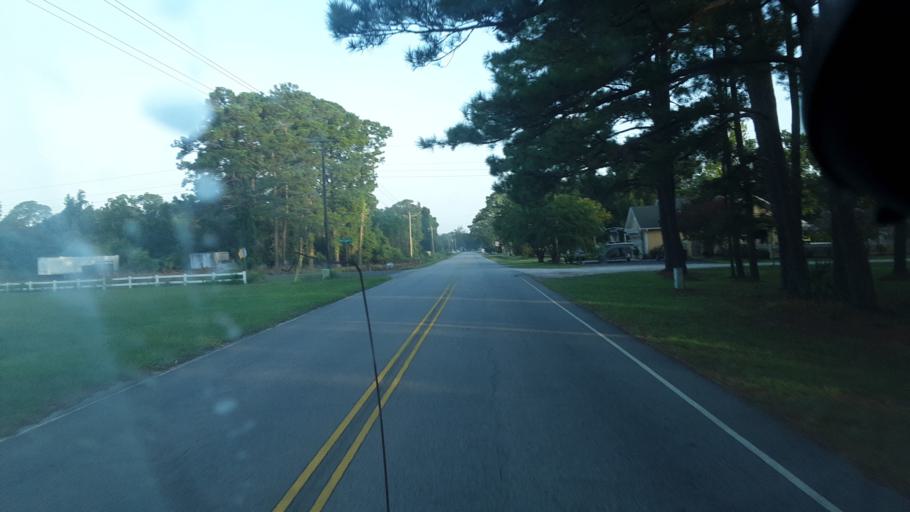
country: US
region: North Carolina
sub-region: Brunswick County
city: Calabash
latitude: 33.8796
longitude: -78.5434
